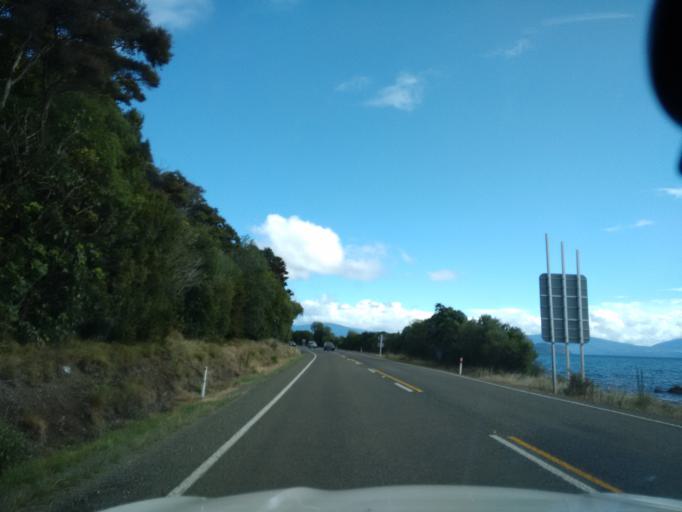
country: NZ
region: Waikato
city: Turangi
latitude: -38.8875
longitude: 175.9530
